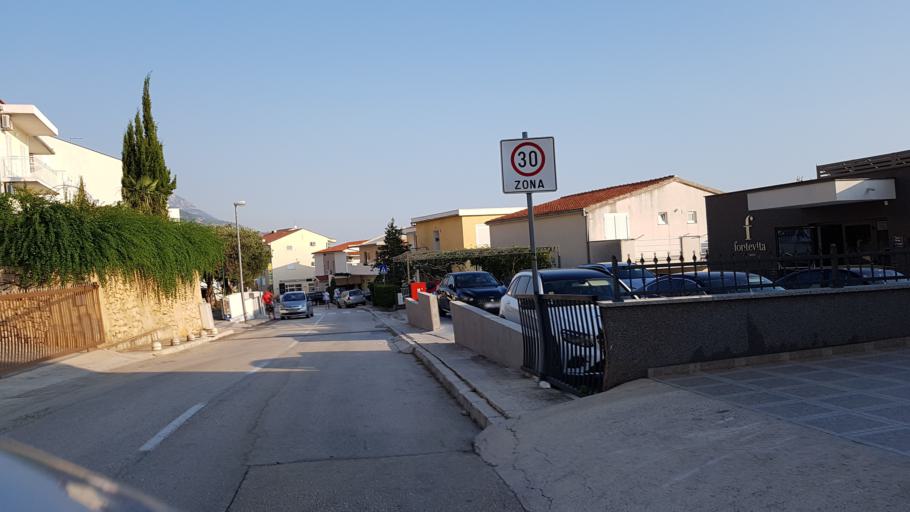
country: HR
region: Splitsko-Dalmatinska
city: Baska Voda
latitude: 43.3610
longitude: 16.9461
